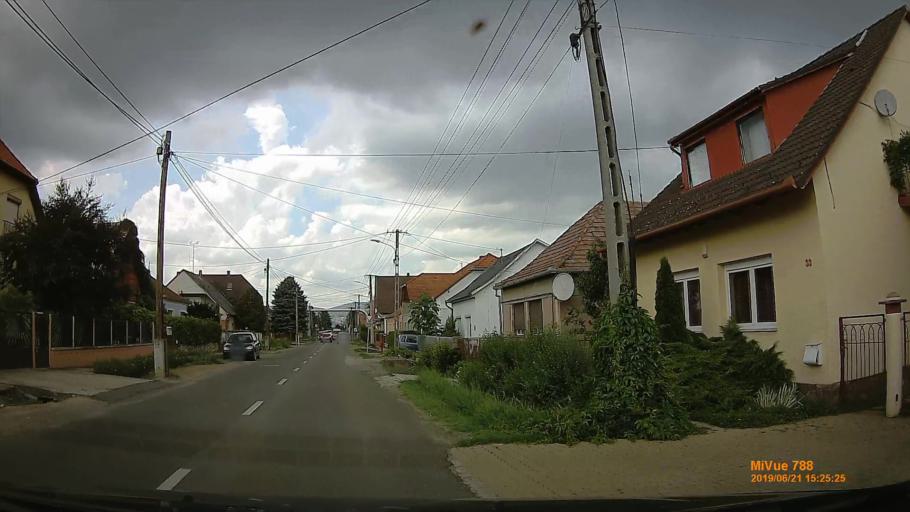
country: HU
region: Baranya
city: Pecs
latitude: 46.0445
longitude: 18.2486
